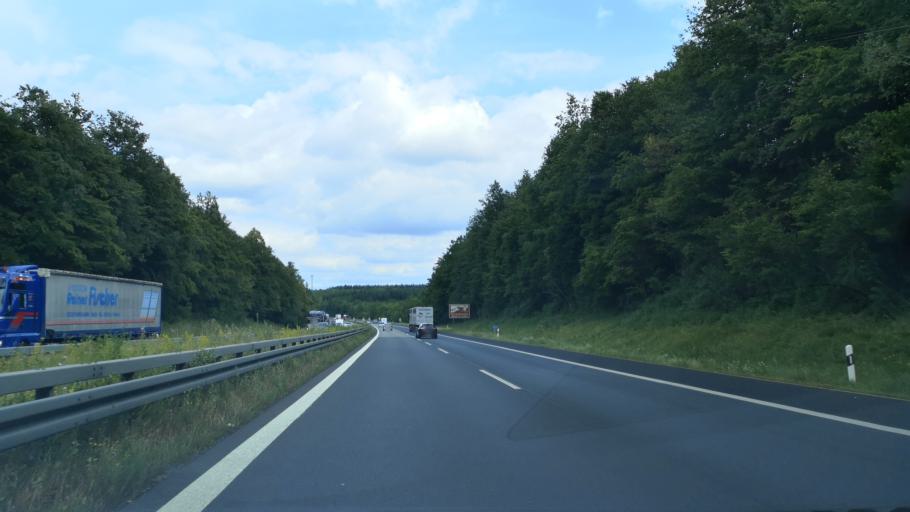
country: DE
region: Bavaria
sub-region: Regierungsbezirk Unterfranken
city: Rottendorf
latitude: 49.8186
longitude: 10.0434
